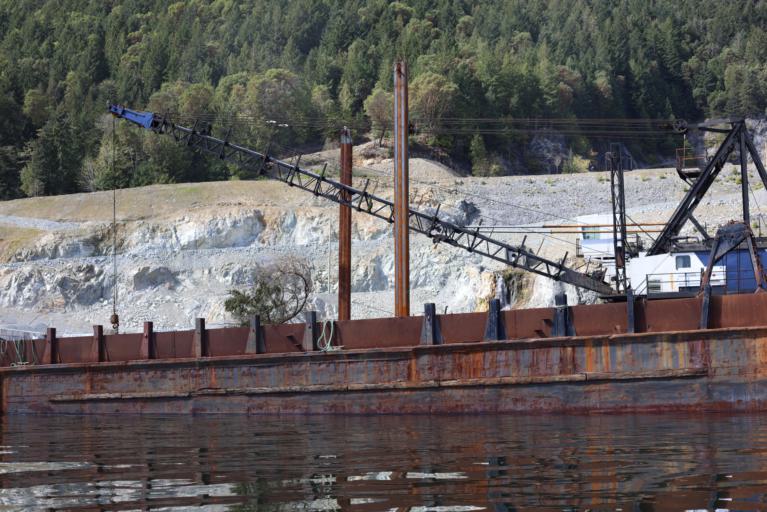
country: CA
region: British Columbia
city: North Saanich
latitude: 48.5854
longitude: -123.5202
